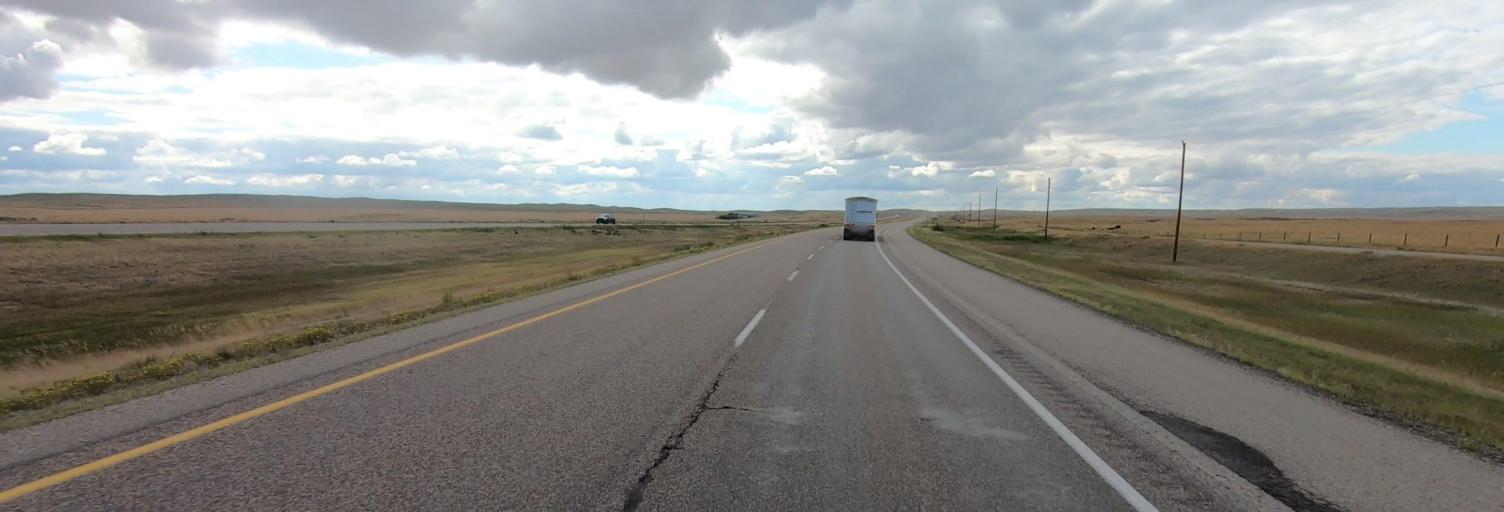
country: CA
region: Saskatchewan
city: Maple Creek
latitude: 49.9608
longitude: -109.7148
